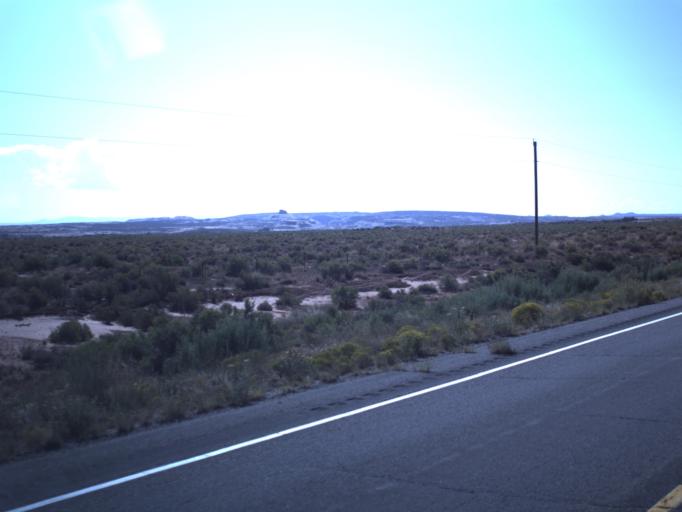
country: US
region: Utah
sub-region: San Juan County
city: Blanding
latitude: 37.1090
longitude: -109.5462
